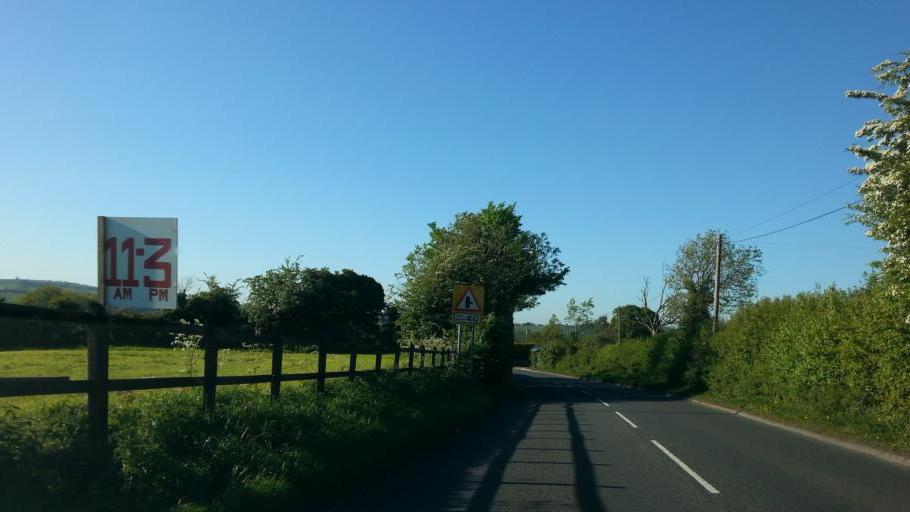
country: GB
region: England
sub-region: Bath and North East Somerset
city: Publow
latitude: 51.3585
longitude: -2.5407
